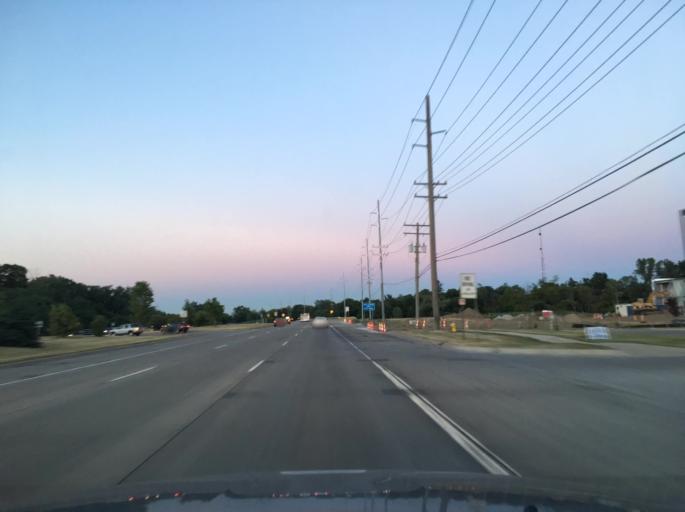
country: US
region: Michigan
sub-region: Macomb County
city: Mount Clemens
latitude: 42.6285
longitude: -82.8937
